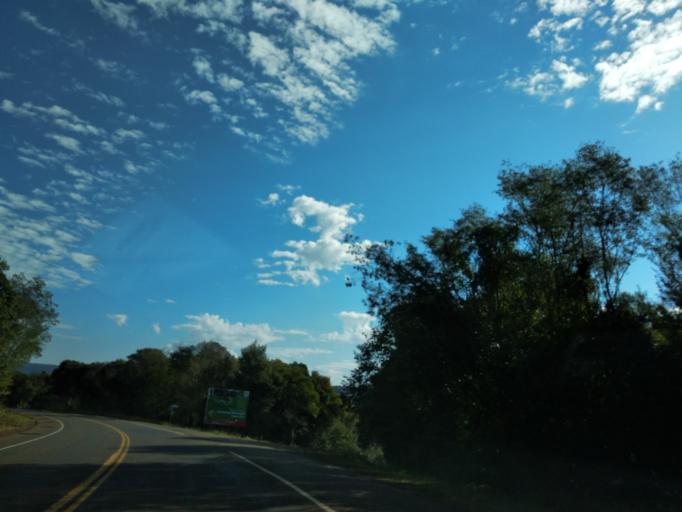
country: AR
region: Misiones
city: Aristobulo del Valle
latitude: -27.0918
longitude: -54.9492
